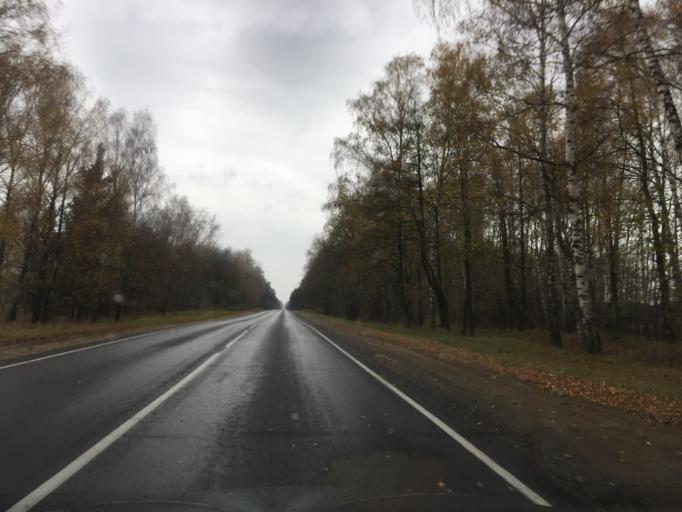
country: BY
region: Mogilev
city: Slawharad
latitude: 53.4166
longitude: 30.9540
